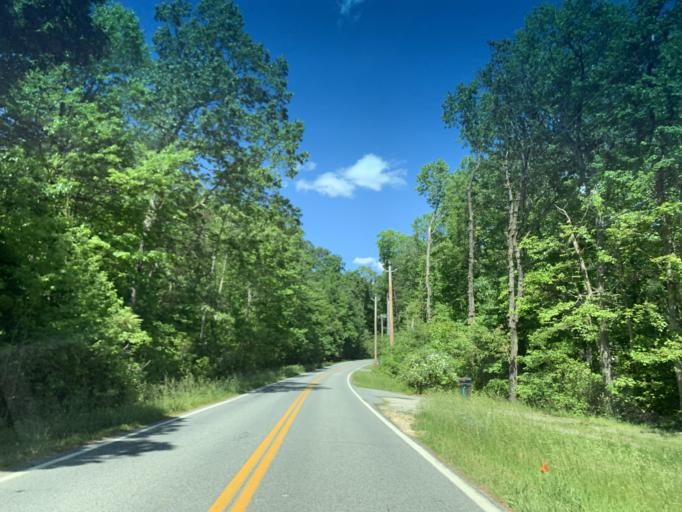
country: US
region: Maryland
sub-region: Cecil County
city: Charlestown
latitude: 39.5383
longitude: -75.9233
